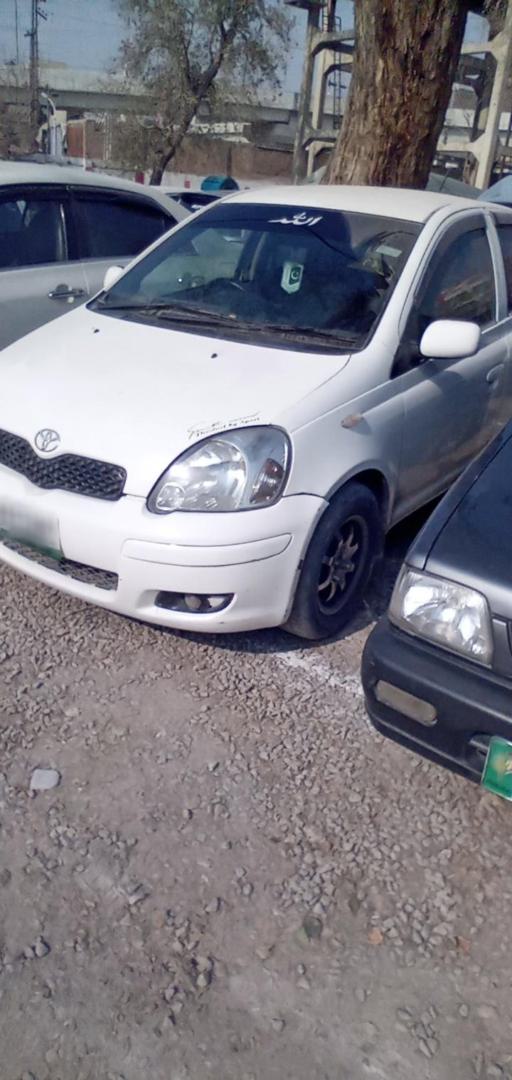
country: PK
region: Khyber Pakhtunkhwa
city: Peshawar
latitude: 33.9950
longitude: 71.5356
